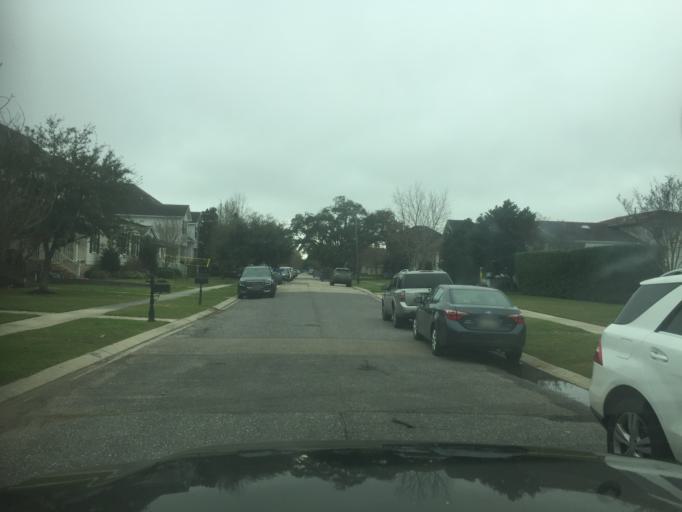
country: US
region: Louisiana
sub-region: Jefferson Parish
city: Metairie
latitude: 30.0081
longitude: -90.1100
